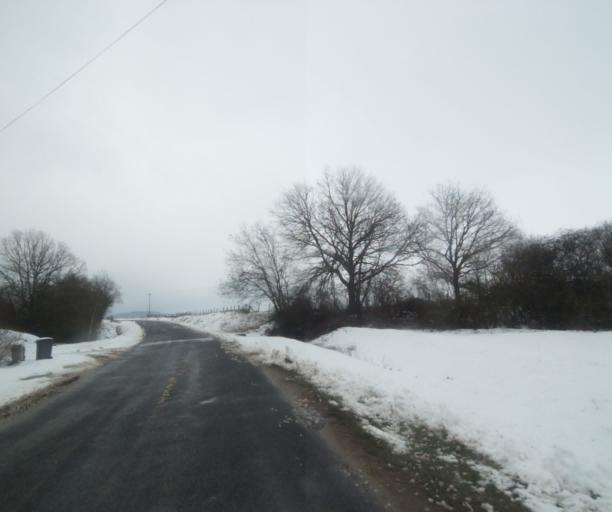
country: FR
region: Champagne-Ardenne
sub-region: Departement de la Haute-Marne
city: Montier-en-Der
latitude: 48.4723
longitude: 4.7879
